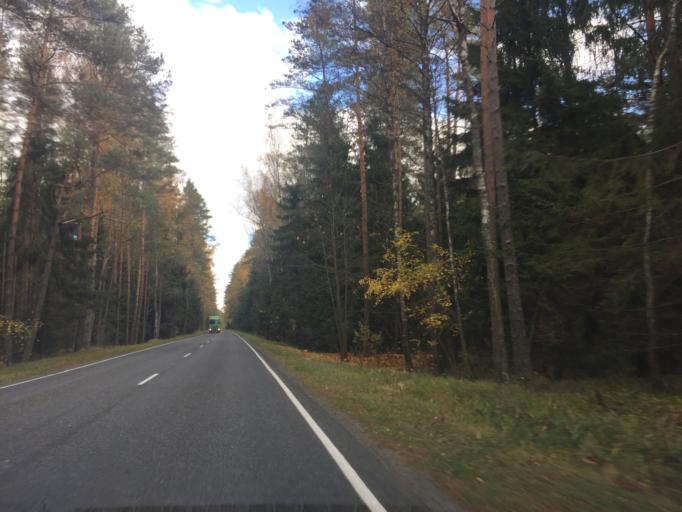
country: BY
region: Minsk
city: Narach
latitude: 54.9417
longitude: 26.5720
